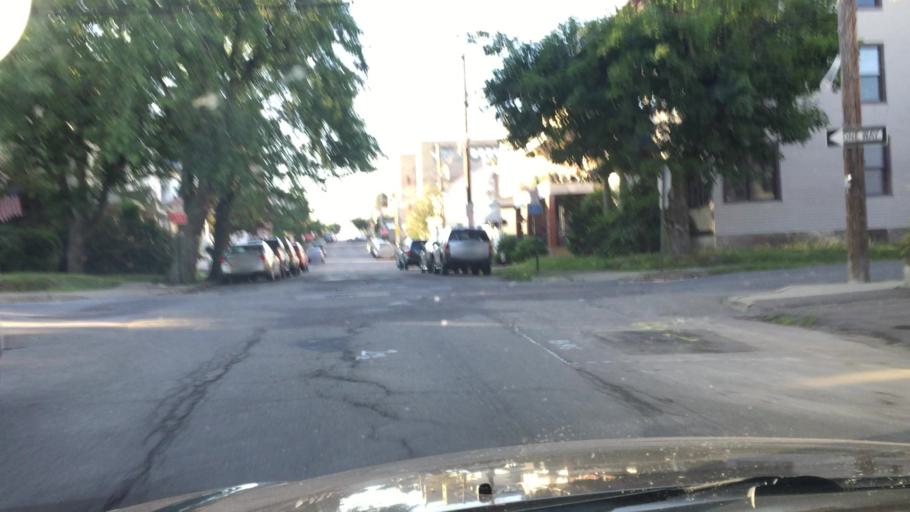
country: US
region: Pennsylvania
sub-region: Luzerne County
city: Hazleton
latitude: 40.9618
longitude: -75.9731
